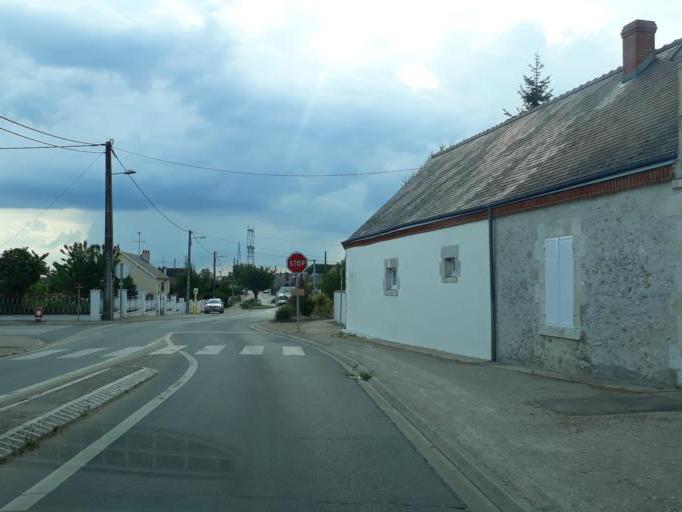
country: FR
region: Centre
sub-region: Departement du Loiret
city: Ingre
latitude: 47.9201
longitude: 1.8075
